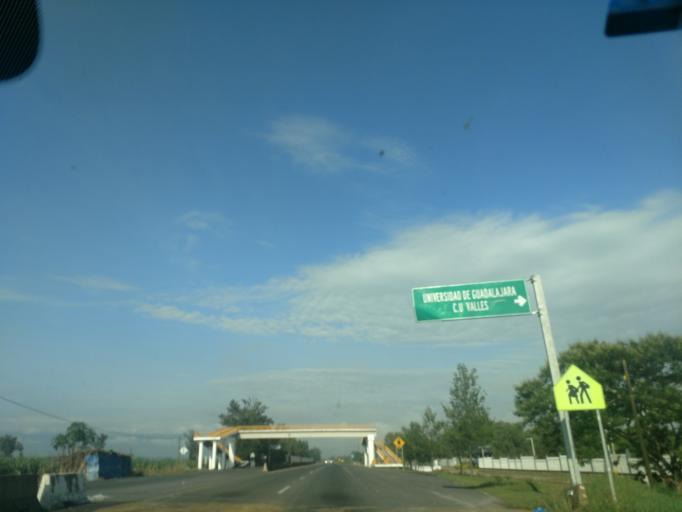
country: MX
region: Jalisco
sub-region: Ameca
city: Los Pocitos
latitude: 20.5344
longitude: -103.9658
